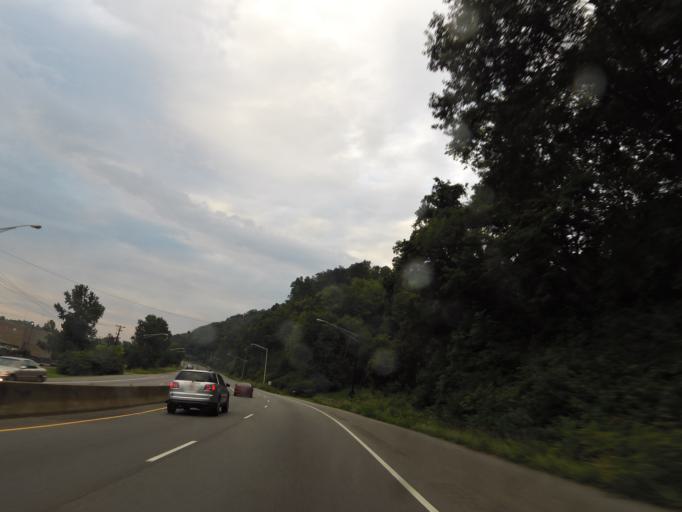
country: US
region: Tennessee
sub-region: Knox County
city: Knoxville
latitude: 35.9286
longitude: -83.9502
